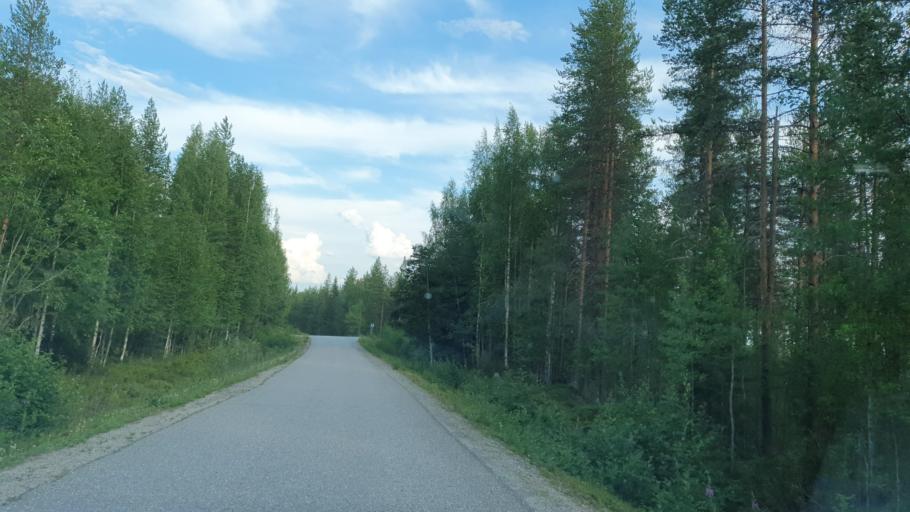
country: FI
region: Kainuu
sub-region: Kehys-Kainuu
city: Kuhmo
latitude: 64.2830
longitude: 29.3939
